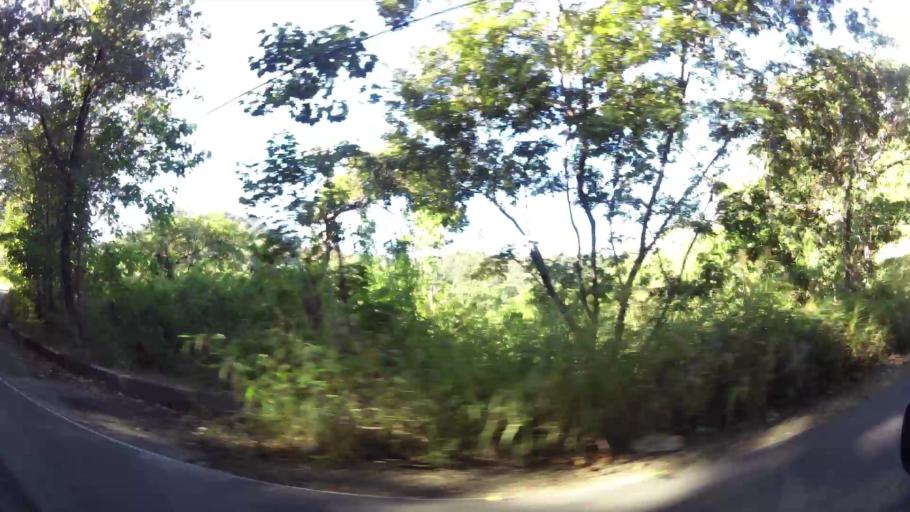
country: CR
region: Guanacaste
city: Belen
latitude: 10.3685
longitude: -85.7587
